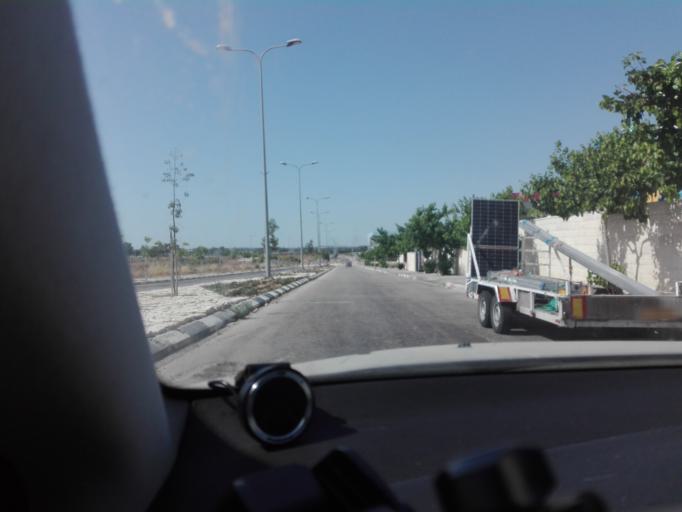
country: IL
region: Central District
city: Bene 'Ayish
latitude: 31.7216
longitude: 34.7570
